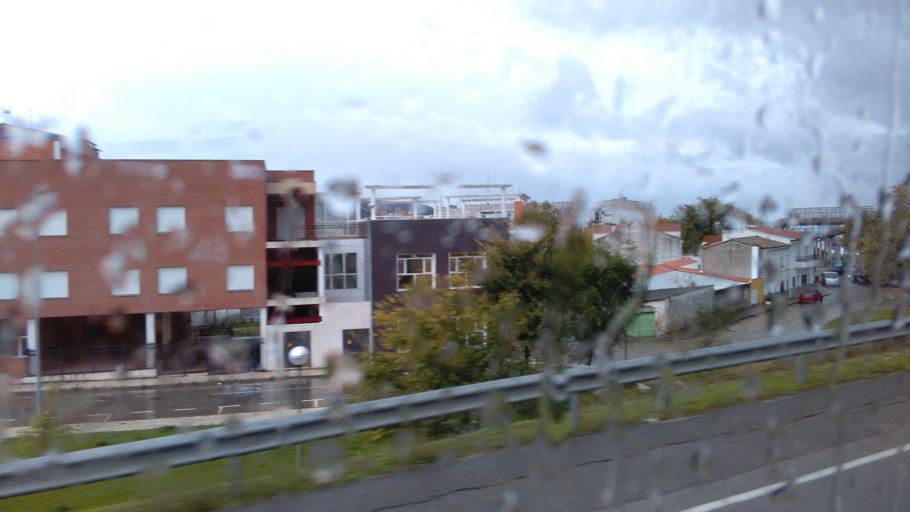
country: ES
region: Extremadura
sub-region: Provincia de Caceres
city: Navalmoral de la Mata
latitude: 39.8960
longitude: -5.5355
